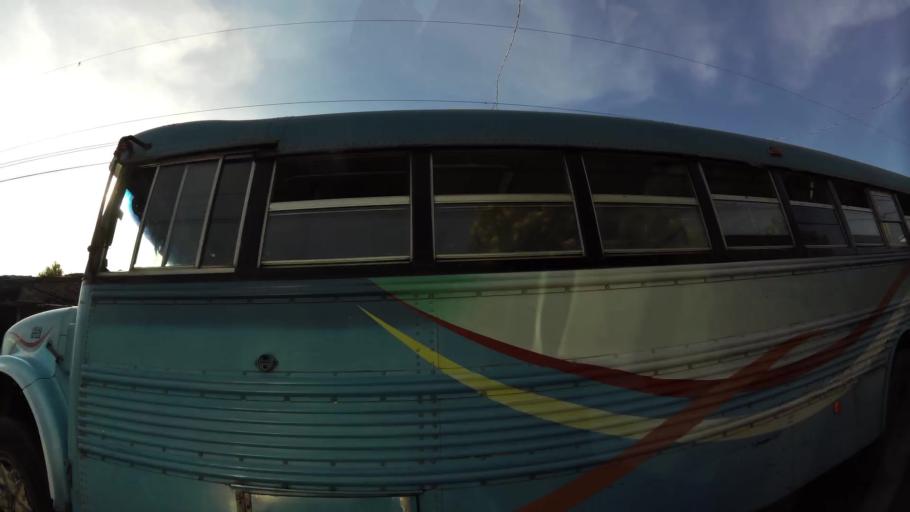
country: SV
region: San Miguel
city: San Miguel
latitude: 13.4652
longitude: -88.1813
